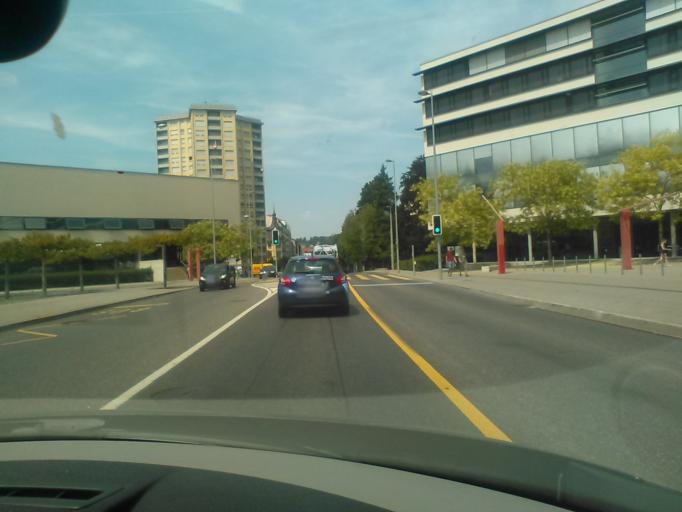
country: CH
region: Fribourg
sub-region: Sarine District
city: Fribourg
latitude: 46.7934
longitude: 7.1587
